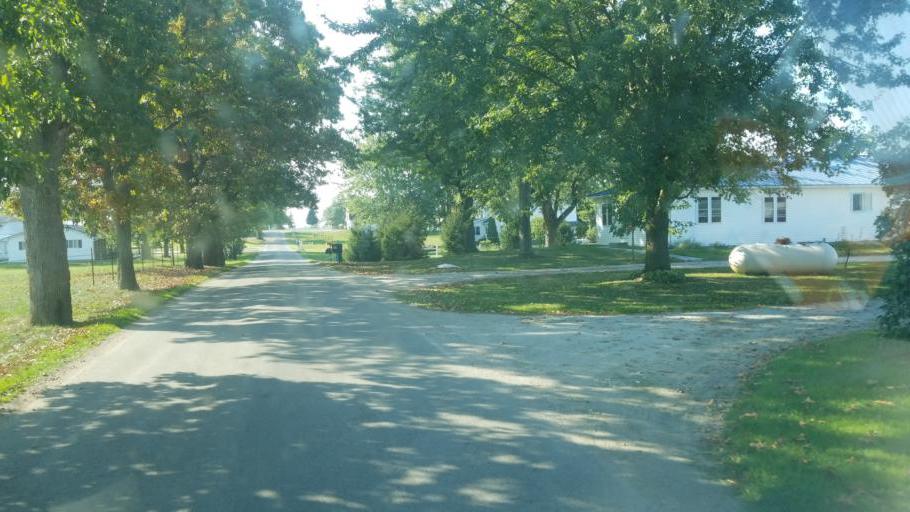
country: US
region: Indiana
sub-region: LaGrange County
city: Topeka
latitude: 41.6716
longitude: -85.5612
